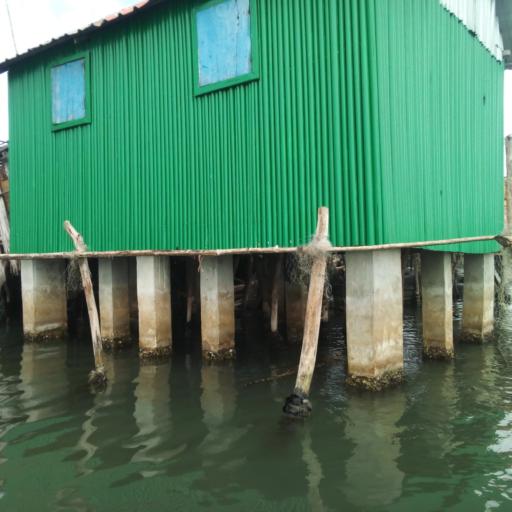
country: BJ
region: Littoral
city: Cotonou
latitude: 6.3907
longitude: 2.4343
